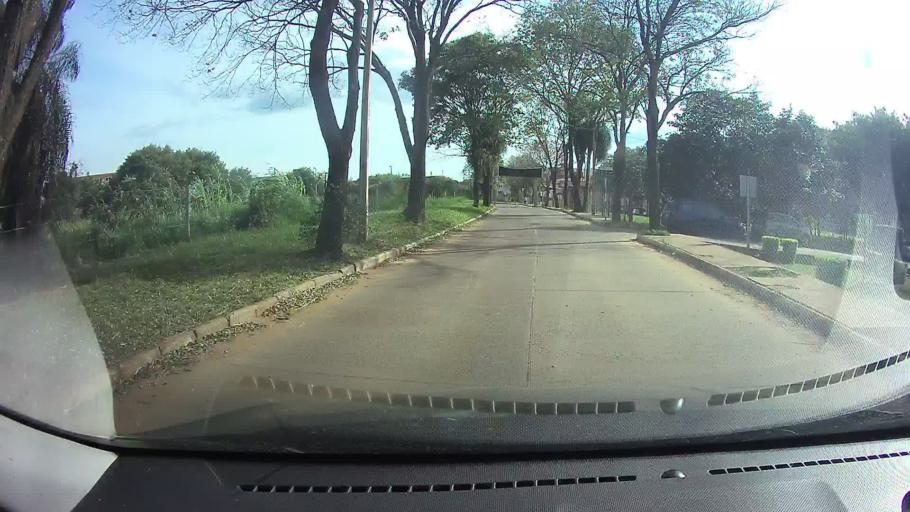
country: PY
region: Central
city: Fernando de la Mora
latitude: -25.3260
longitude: -57.5240
